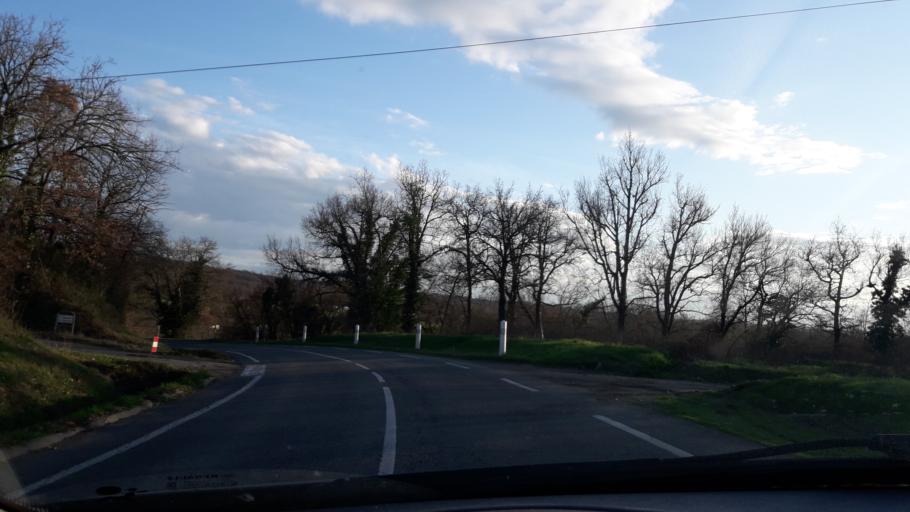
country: FR
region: Midi-Pyrenees
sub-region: Departement de la Haute-Garonne
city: Montaigut-sur-Save
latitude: 43.7230
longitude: 1.2455
